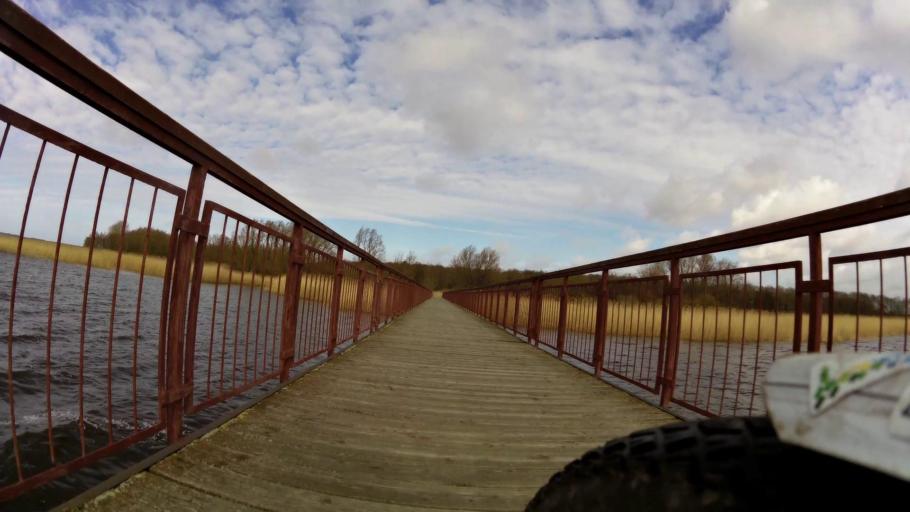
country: PL
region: West Pomeranian Voivodeship
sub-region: Powiat kamienski
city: Kamien Pomorski
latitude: 53.9765
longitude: 14.7713
